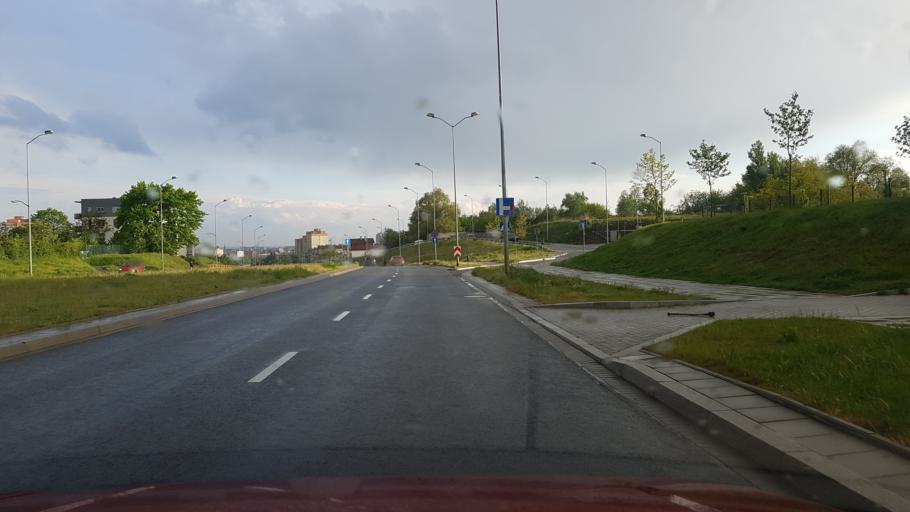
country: PL
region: West Pomeranian Voivodeship
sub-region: Szczecin
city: Szczecin
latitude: 53.4586
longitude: 14.5517
